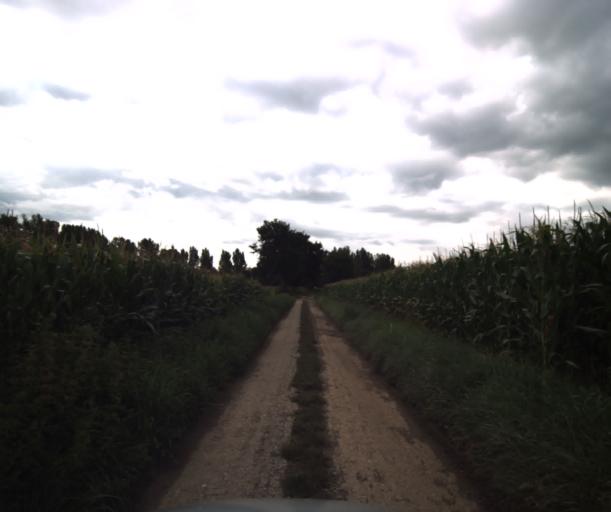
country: FR
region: Midi-Pyrenees
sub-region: Departement de la Haute-Garonne
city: Longages
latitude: 43.3807
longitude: 1.2307
